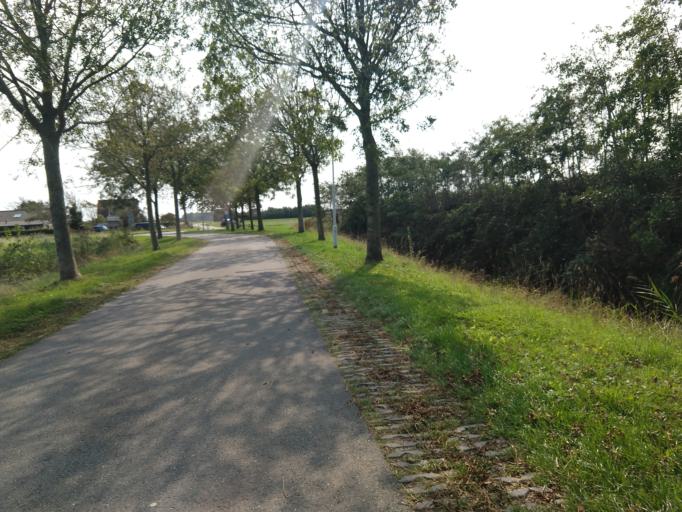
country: NL
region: Zeeland
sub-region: Schouwen-Duiveland
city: Renesse
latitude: 51.7159
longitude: 3.7930
